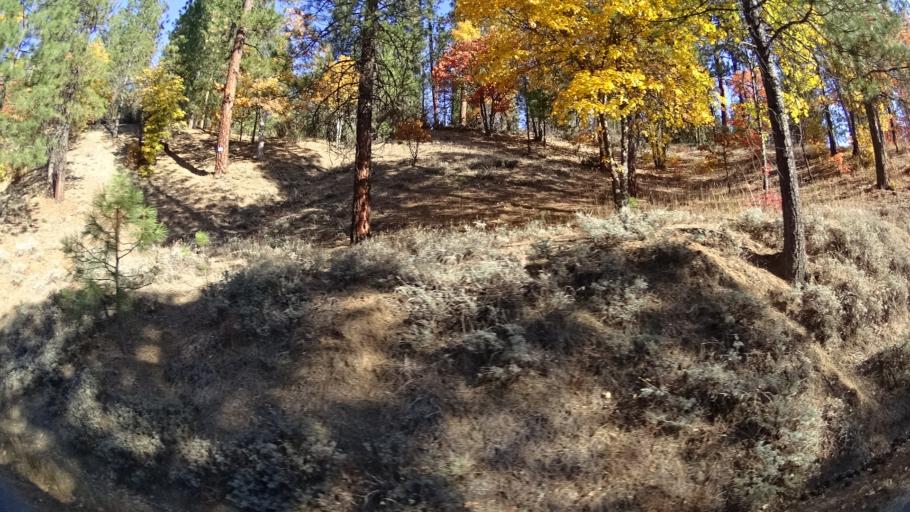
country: US
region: California
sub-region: Siskiyou County
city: Yreka
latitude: 41.6416
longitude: -122.9977
